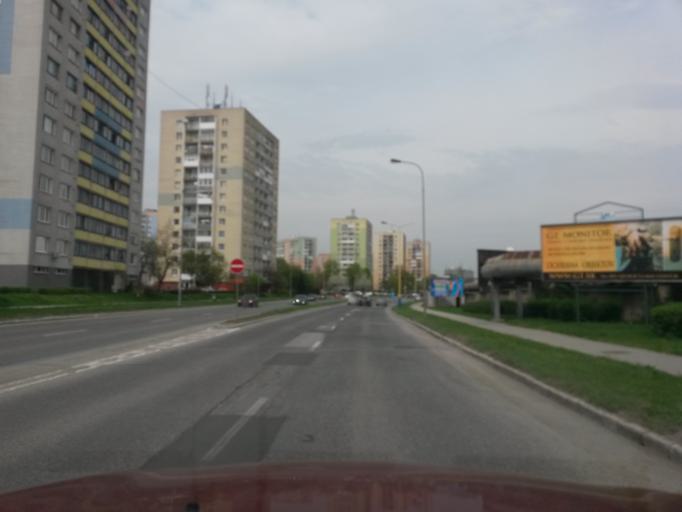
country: SK
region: Kosicky
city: Kosice
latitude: 48.7110
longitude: 21.2652
